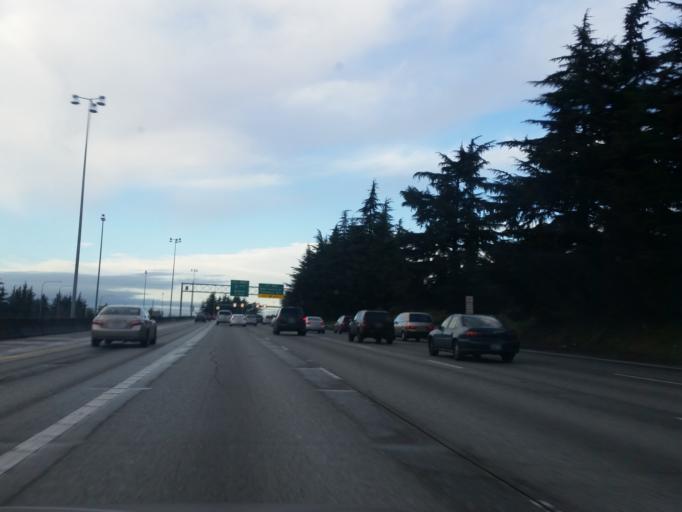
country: US
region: Washington
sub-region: King County
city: White Center
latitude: 47.5553
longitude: -122.3187
